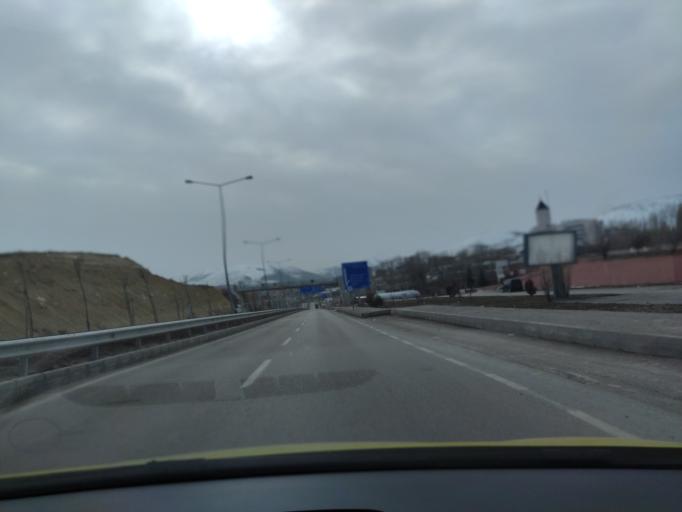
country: TR
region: Bayburt
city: Bayburt
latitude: 40.2630
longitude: 40.2073
